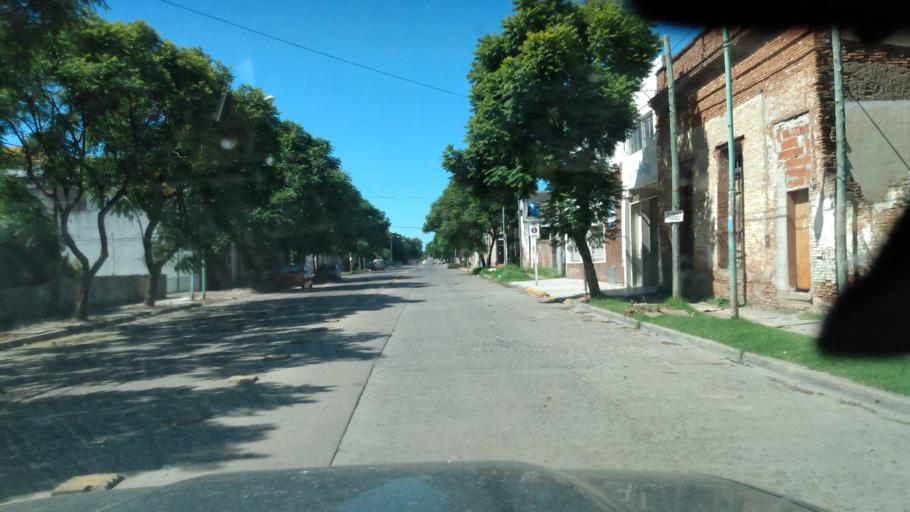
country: AR
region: Buenos Aires
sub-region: Partido de Lujan
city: Lujan
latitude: -34.5700
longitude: -59.1181
